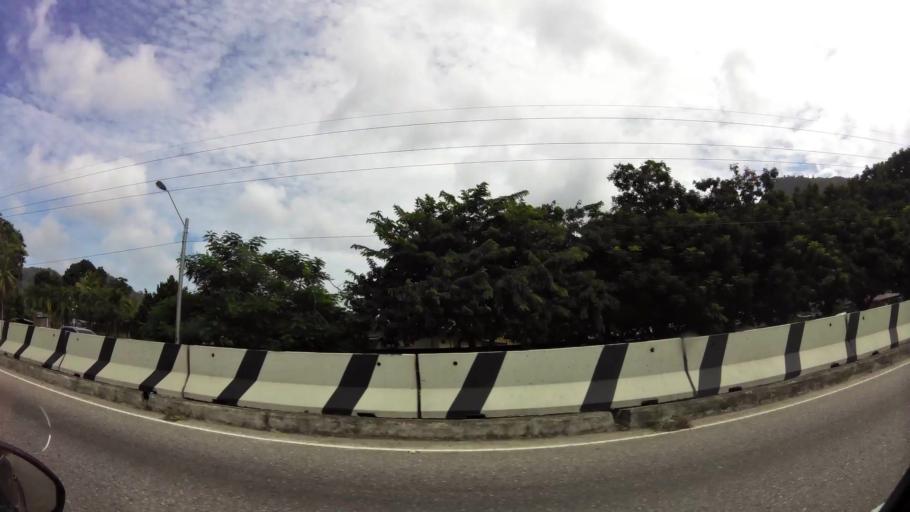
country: TT
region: Diego Martin
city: Petit Valley
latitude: 10.7039
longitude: -61.5536
